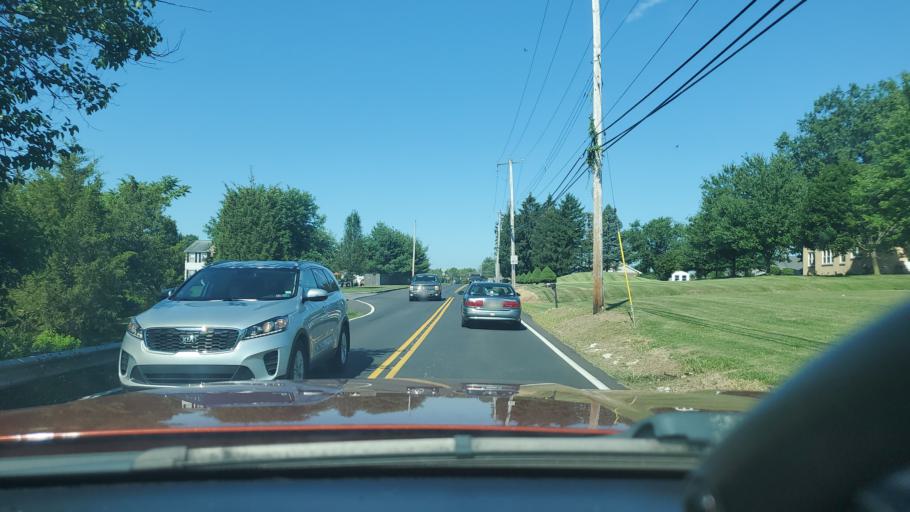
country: US
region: Pennsylvania
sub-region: Montgomery County
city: Limerick
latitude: 40.2477
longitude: -75.5307
